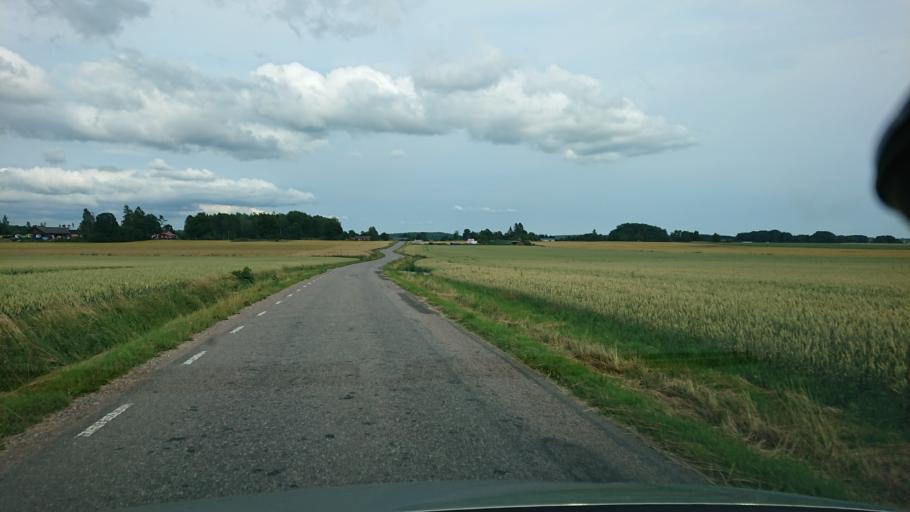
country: SE
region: Uppsala
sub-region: Osthammars Kommun
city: Bjorklinge
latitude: 59.9905
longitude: 17.5149
